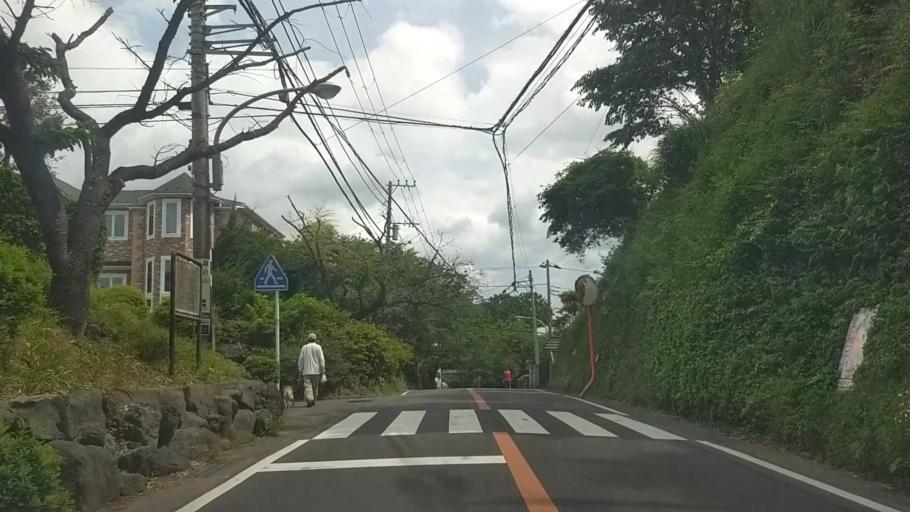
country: JP
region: Kanagawa
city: Kamakura
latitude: 35.3188
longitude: 139.5201
